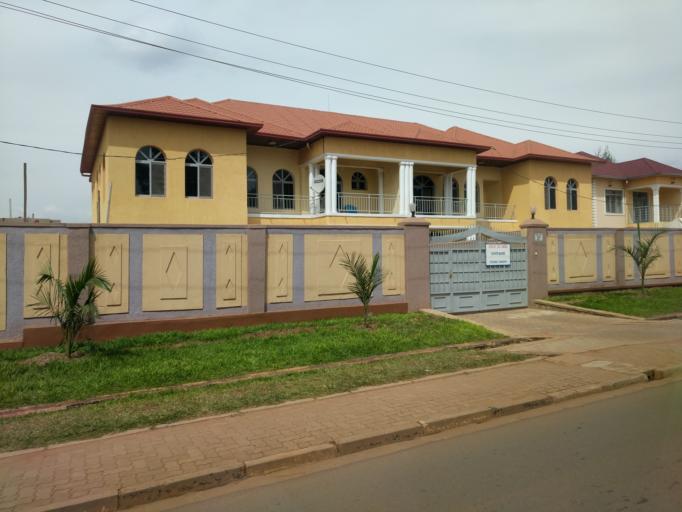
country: RW
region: Kigali
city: Kigali
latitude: -1.9759
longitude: 30.1087
